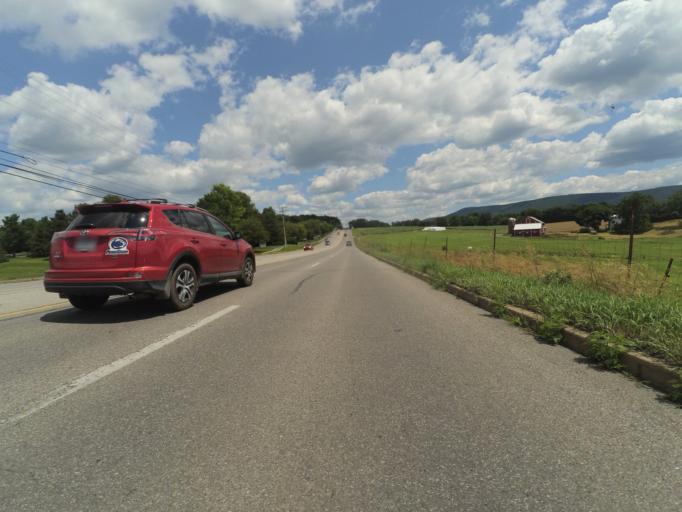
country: US
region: Pennsylvania
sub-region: Centre County
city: Lemont
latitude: 40.7839
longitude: -77.8238
